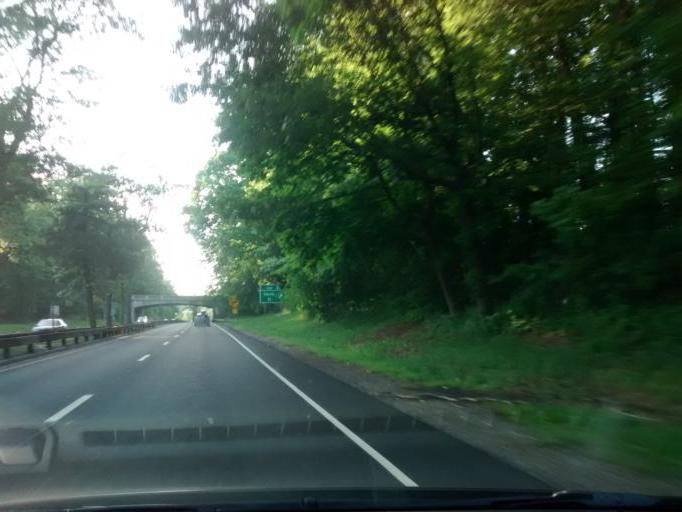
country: US
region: Connecticut
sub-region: Fairfield County
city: Glenville
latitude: 41.0933
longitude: -73.6307
